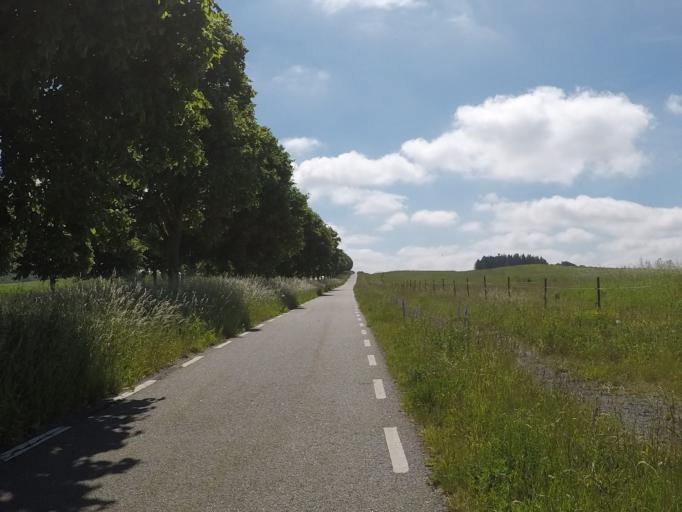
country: SE
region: Skane
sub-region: Svedala Kommun
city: Klagerup
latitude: 55.5723
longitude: 13.1990
